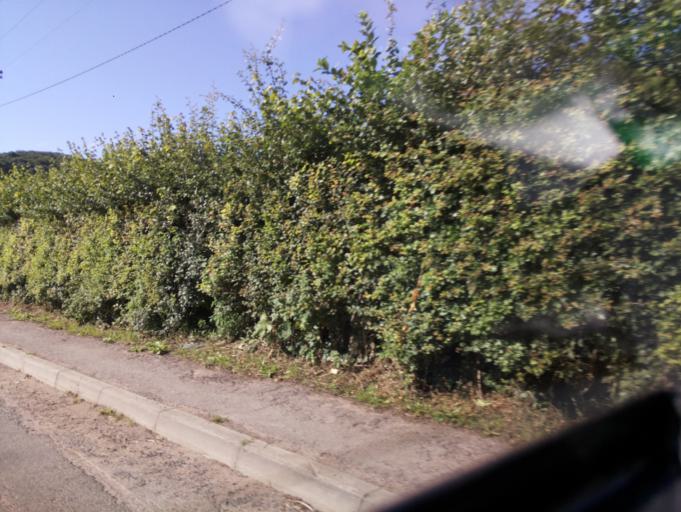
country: GB
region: England
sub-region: Herefordshire
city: Walford
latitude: 51.8809
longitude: -2.6007
